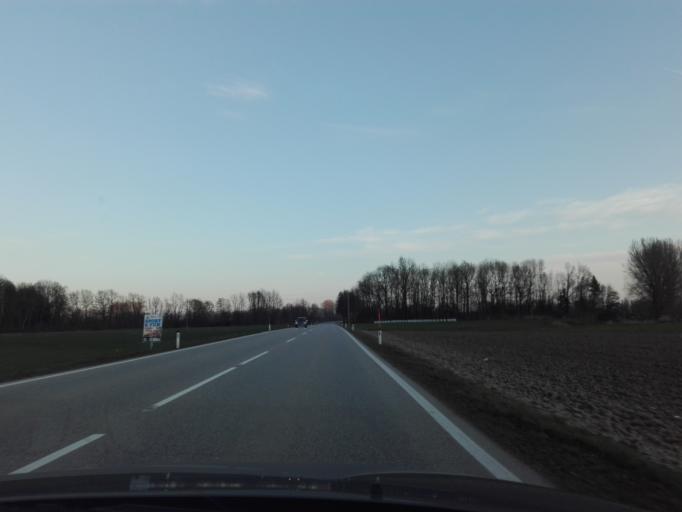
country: AT
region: Upper Austria
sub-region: Politischer Bezirk Urfahr-Umgebung
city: Feldkirchen an der Donau
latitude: 48.3704
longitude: 13.9779
